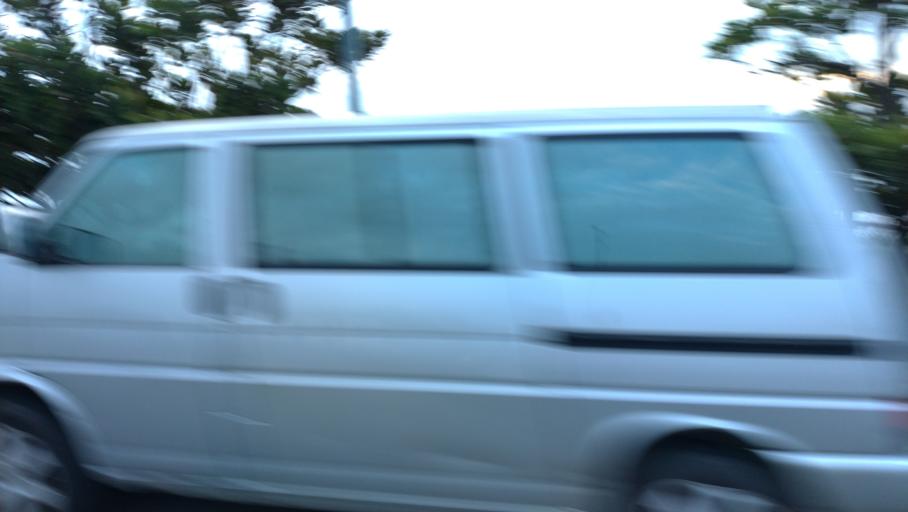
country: TW
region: Taiwan
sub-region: Hsinchu
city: Hsinchu
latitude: 24.7773
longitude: 120.9144
